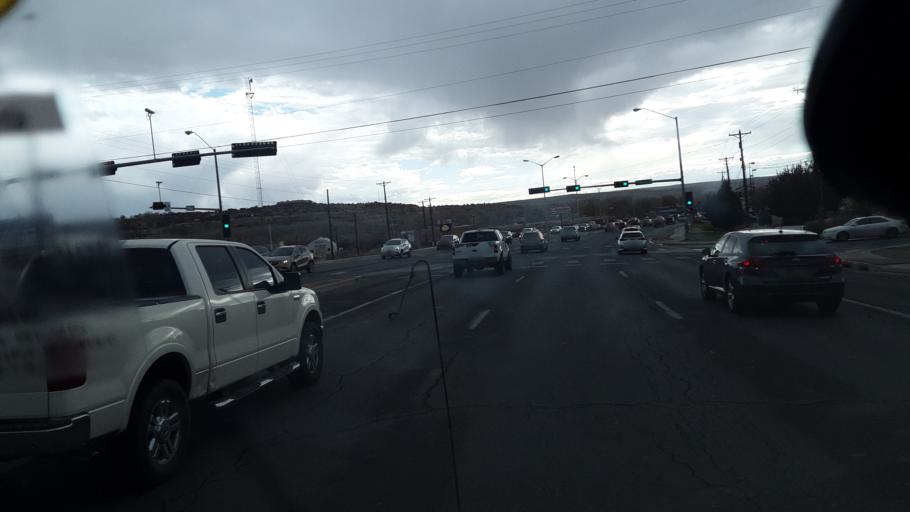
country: US
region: New Mexico
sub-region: San Juan County
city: Farmington
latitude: 36.7531
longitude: -108.1571
